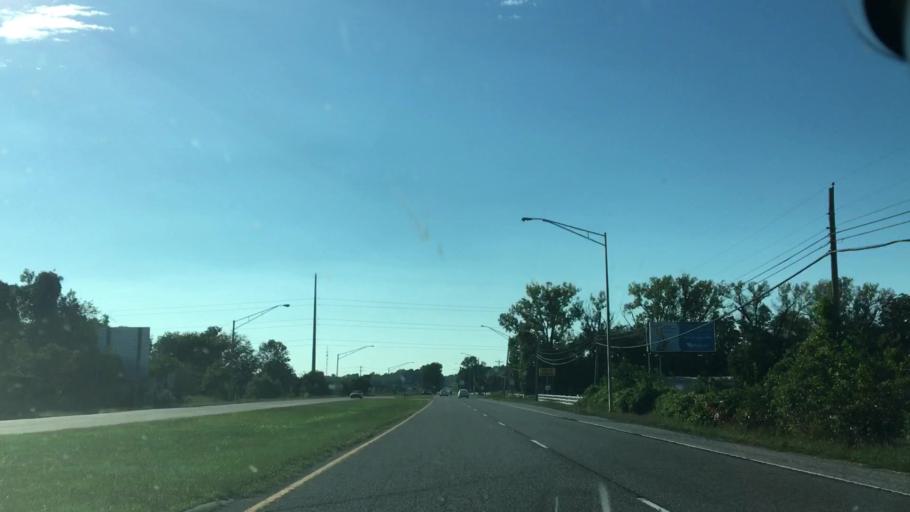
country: US
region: Kentucky
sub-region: Daviess County
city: Owensboro
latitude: 37.7758
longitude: -87.1680
